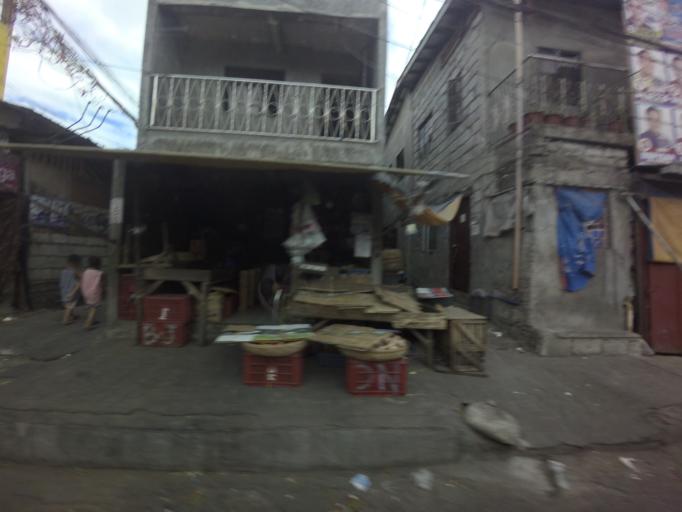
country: PH
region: Calabarzon
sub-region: Province of Rizal
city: Pateros
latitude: 14.5596
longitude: 121.0854
